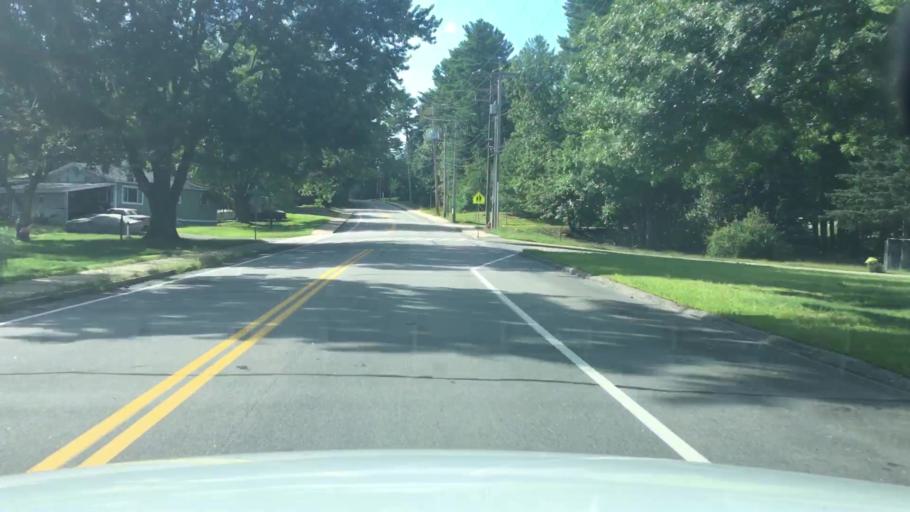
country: US
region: New Hampshire
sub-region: Strafford County
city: Dover
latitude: 43.1640
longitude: -70.8689
